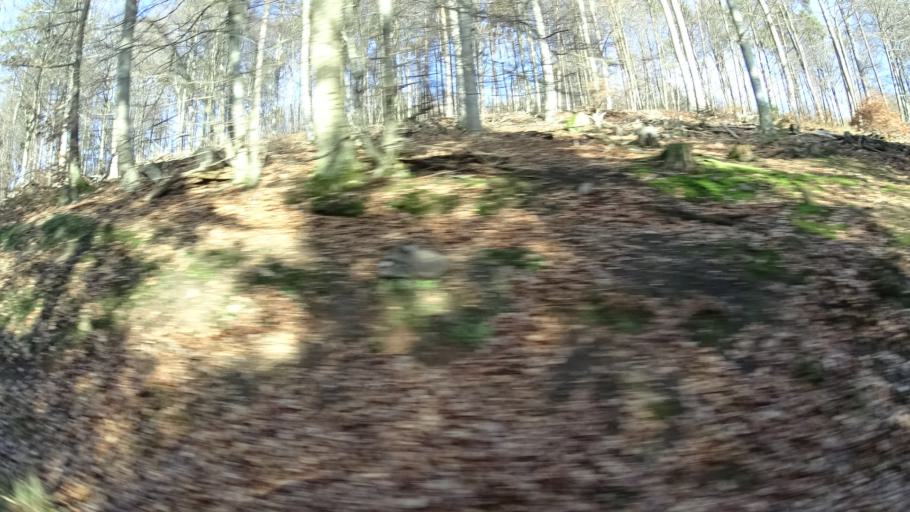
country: DE
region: Baden-Wuerttemberg
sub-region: Regierungsbezirk Stuttgart
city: Freudenberg
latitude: 49.7919
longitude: 9.3117
